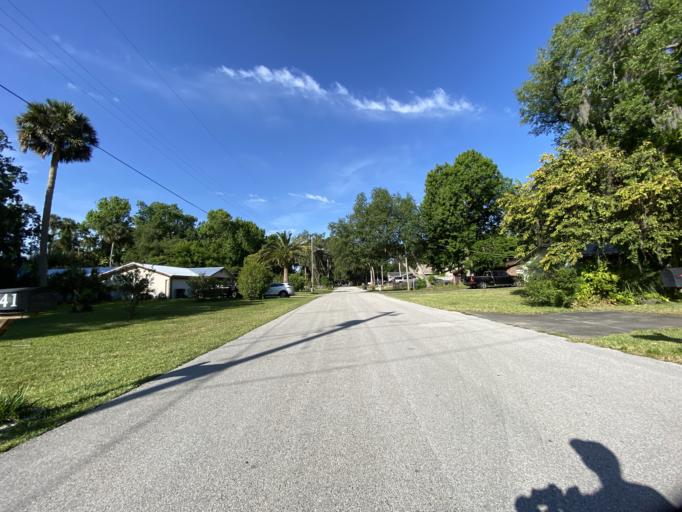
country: US
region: Florida
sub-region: Volusia County
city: South Daytona
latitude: 29.1761
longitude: -81.0188
